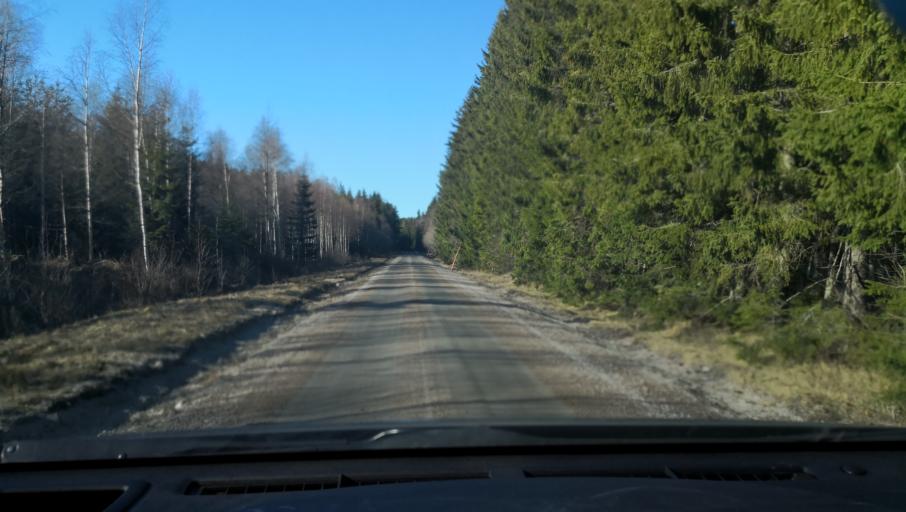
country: SE
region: Vaestmanland
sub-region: Sala Kommun
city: Sala
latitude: 60.1387
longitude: 16.6491
